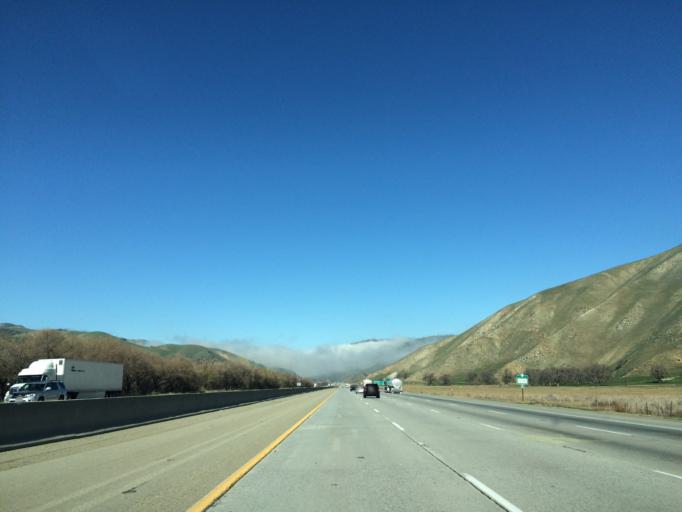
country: US
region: California
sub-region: Kern County
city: Lebec
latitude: 34.8422
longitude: -118.8649
